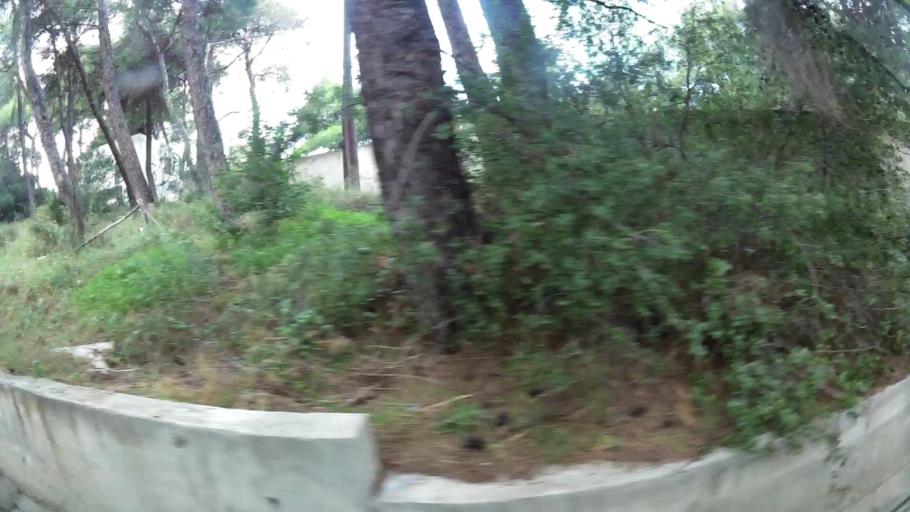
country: GR
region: Attica
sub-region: Nomarchia Athinas
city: Melissia
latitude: 38.0582
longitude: 23.8249
